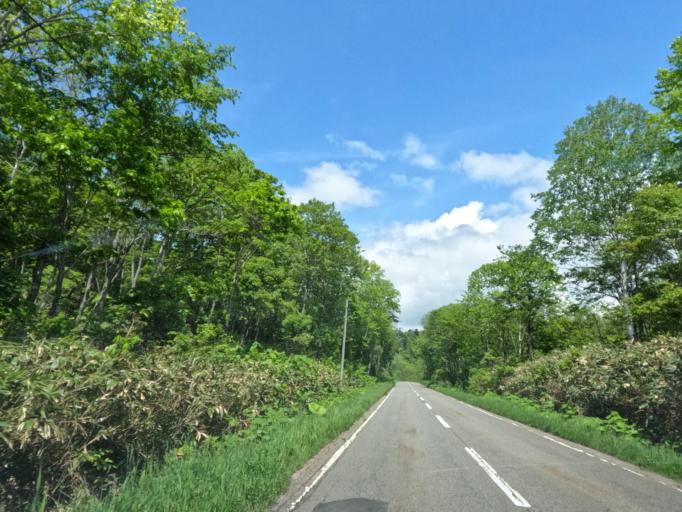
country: JP
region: Hokkaido
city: Takikawa
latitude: 43.5418
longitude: 141.6132
